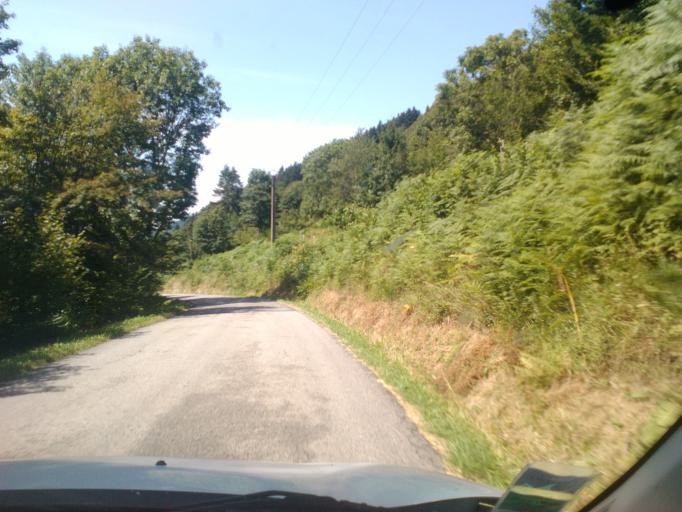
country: FR
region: Lorraine
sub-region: Departement des Vosges
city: La Bresse
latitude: 48.0393
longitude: 6.8217
